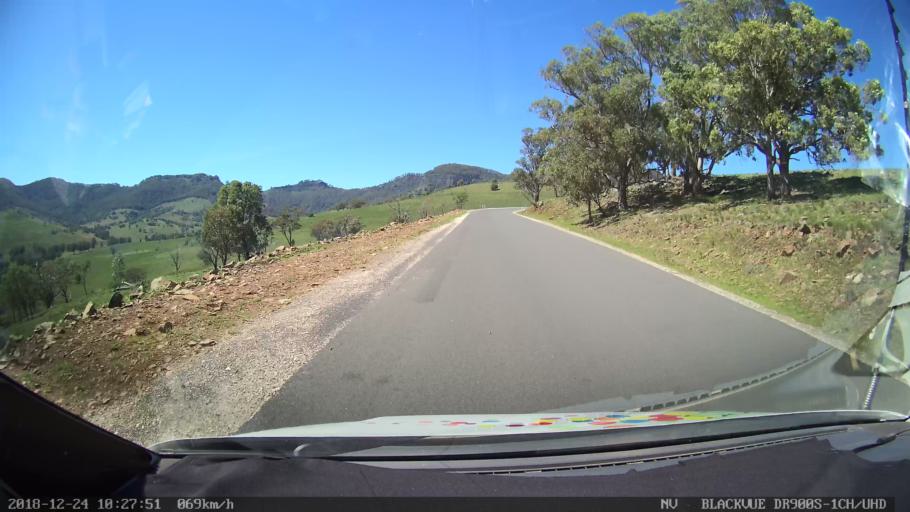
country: AU
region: New South Wales
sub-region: Liverpool Plains
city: Quirindi
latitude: -31.8218
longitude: 150.5338
